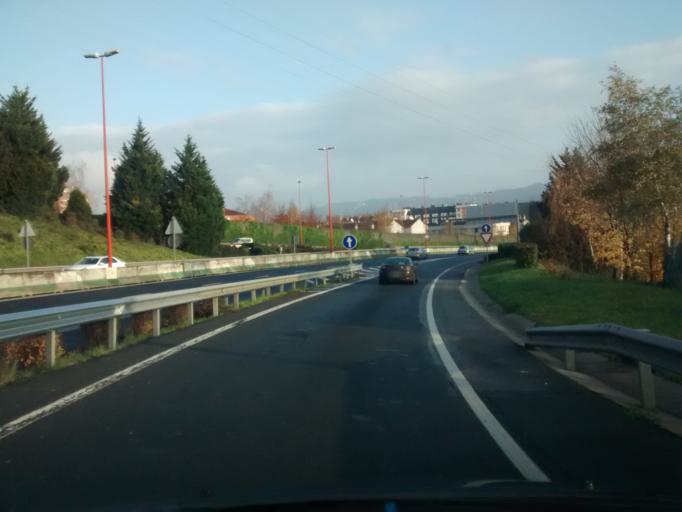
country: ES
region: Basque Country
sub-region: Bizkaia
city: Santutxu
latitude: 43.2444
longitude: -2.9302
